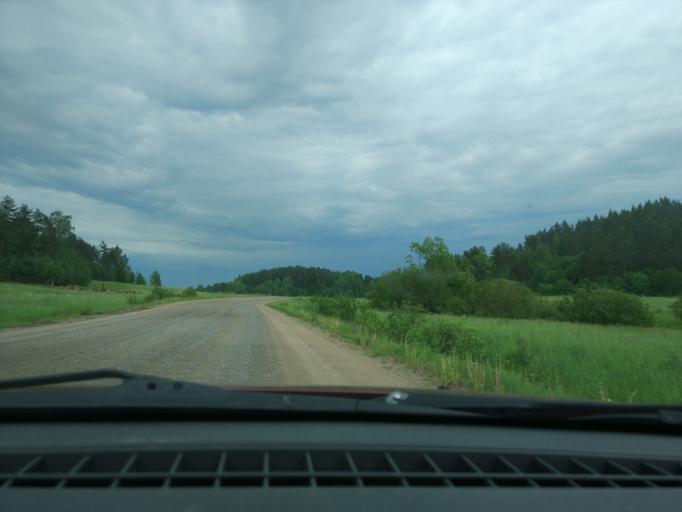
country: RU
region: Leningrad
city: Kuznechnoye
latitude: 61.2785
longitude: 29.8498
